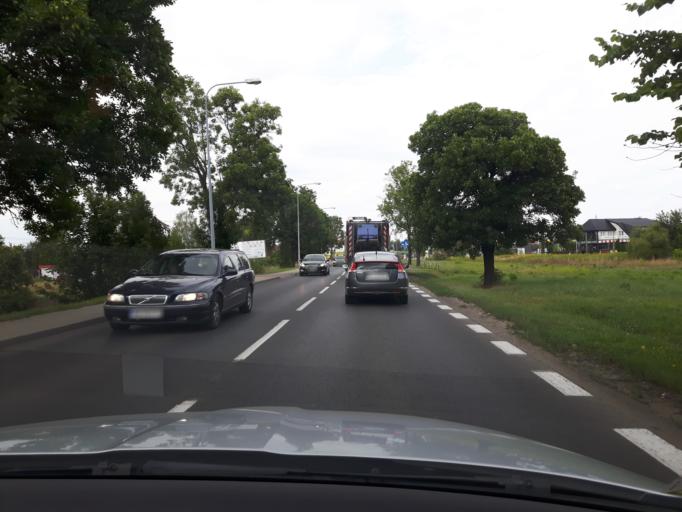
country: PL
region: Masovian Voivodeship
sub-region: Powiat legionowski
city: Stanislawow Pierwszy
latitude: 52.3611
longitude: 21.0282
